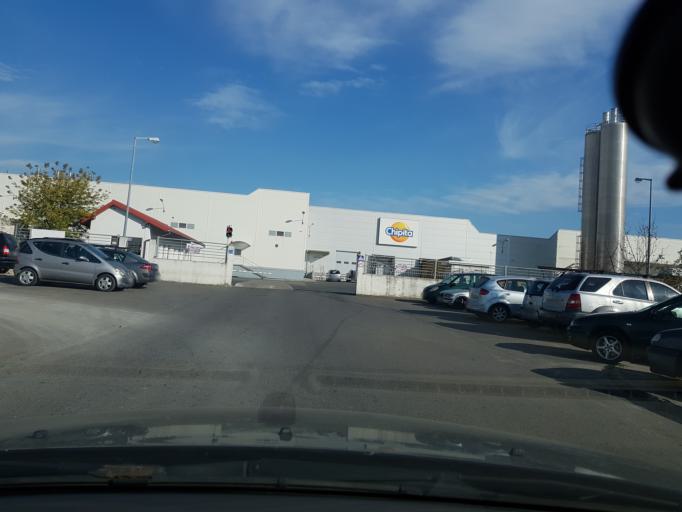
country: PL
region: Lodz Voivodeship
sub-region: Powiat tomaszowski
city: Tomaszow Mazowiecki
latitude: 51.5573
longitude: 20.0253
